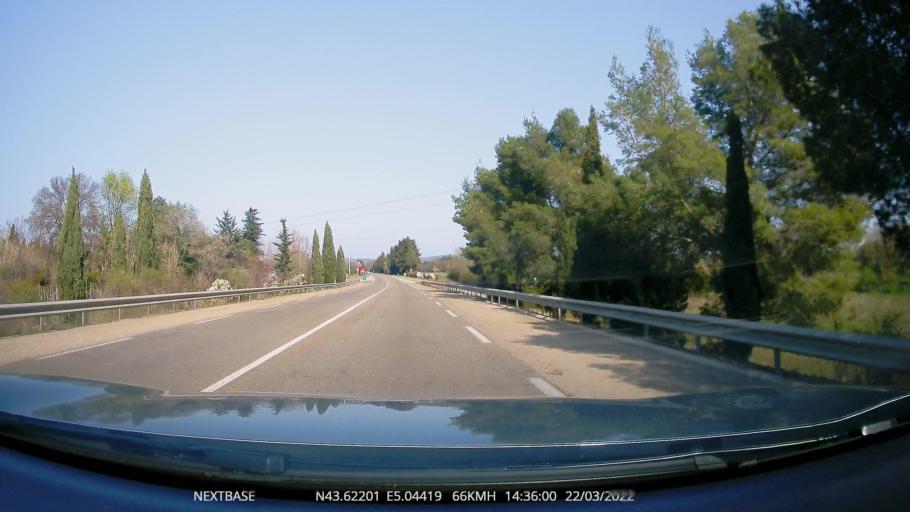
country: FR
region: Provence-Alpes-Cote d'Azur
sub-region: Departement des Bouches-du-Rhone
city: Grans
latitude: 43.6220
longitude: 5.0443
